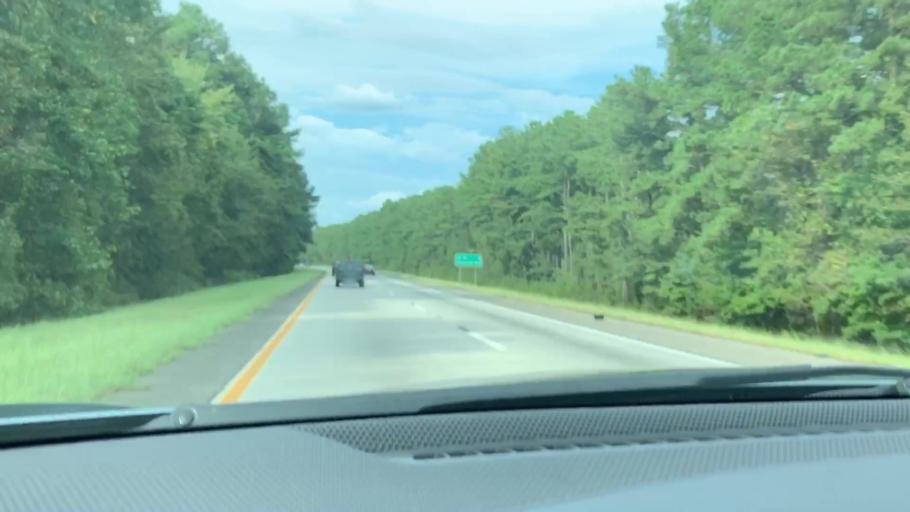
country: US
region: South Carolina
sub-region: Colleton County
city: Walterboro
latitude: 33.0165
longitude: -80.6660
